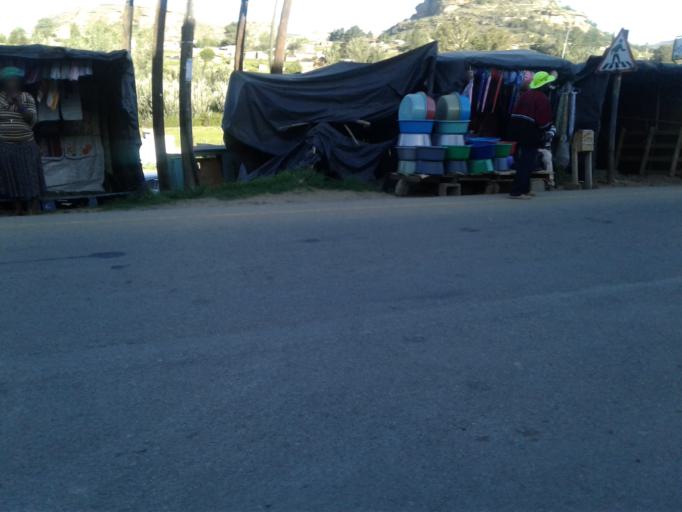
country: LS
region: Butha-Buthe
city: Butha-Buthe
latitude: -28.7658
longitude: 28.2518
